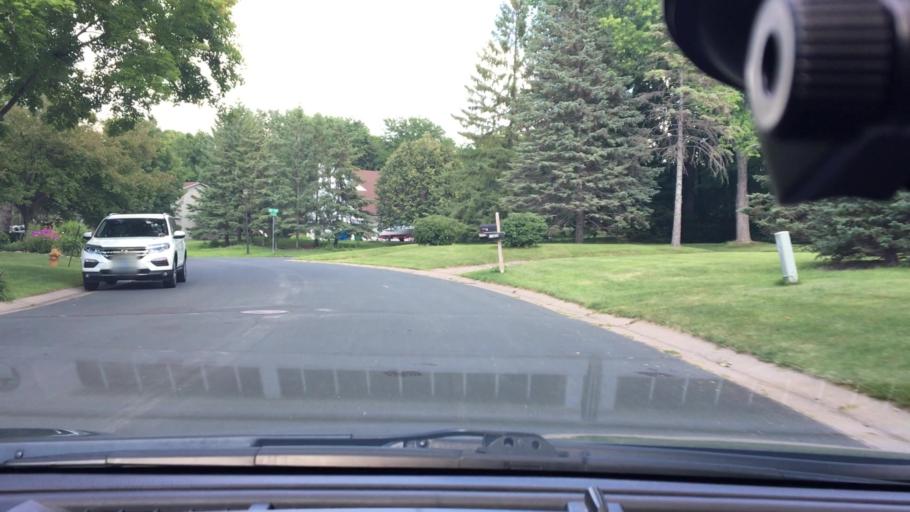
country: US
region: Minnesota
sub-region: Hennepin County
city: Plymouth
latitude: 45.0368
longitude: -93.4318
